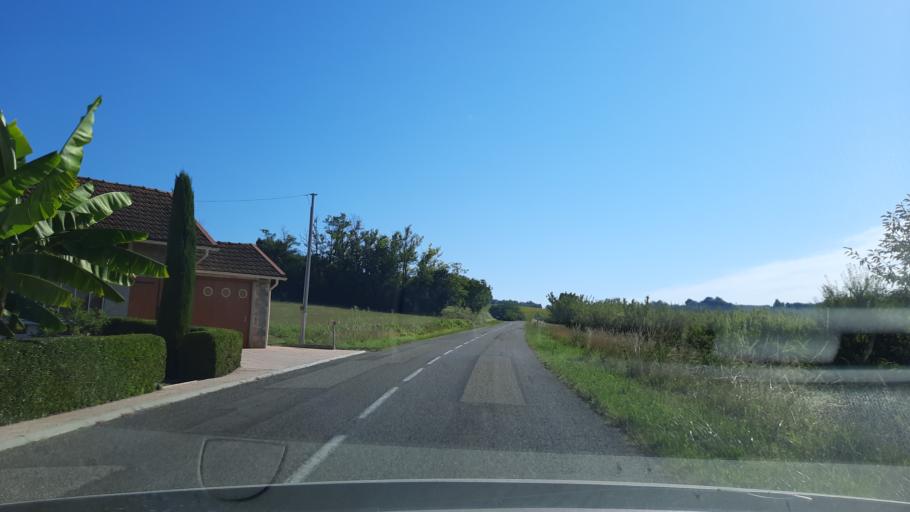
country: FR
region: Midi-Pyrenees
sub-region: Departement du Tarn-et-Garonne
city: Molieres
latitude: 44.1806
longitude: 1.3420
